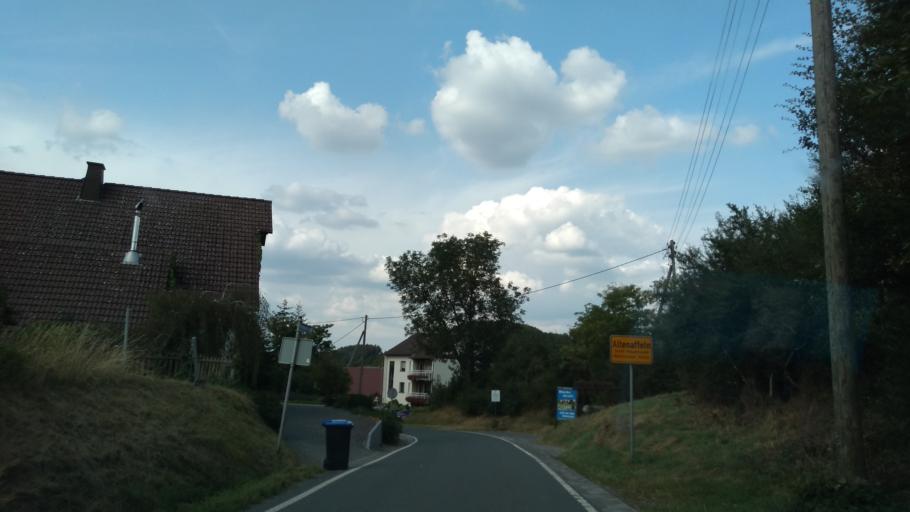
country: DE
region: North Rhine-Westphalia
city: Plettenberg
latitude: 51.2698
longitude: 7.8764
